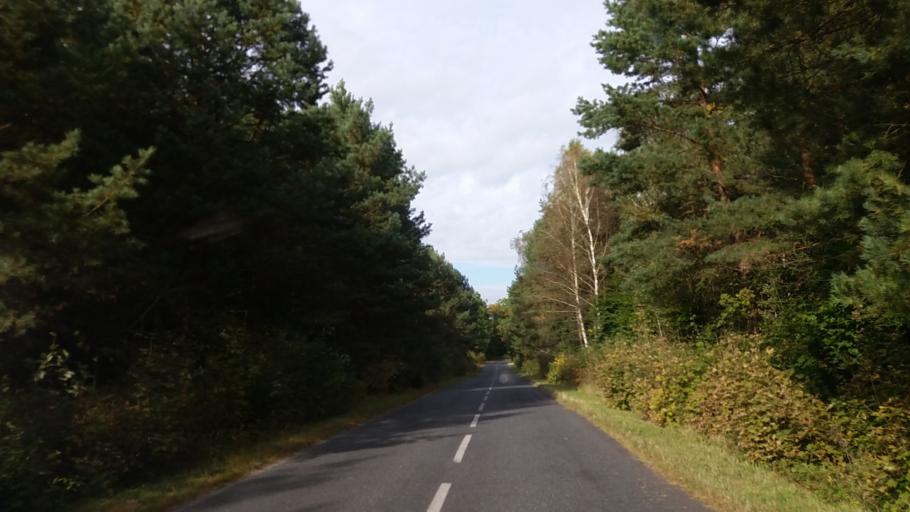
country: PL
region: West Pomeranian Voivodeship
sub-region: Powiat choszczenski
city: Krzecin
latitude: 53.0100
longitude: 15.5019
